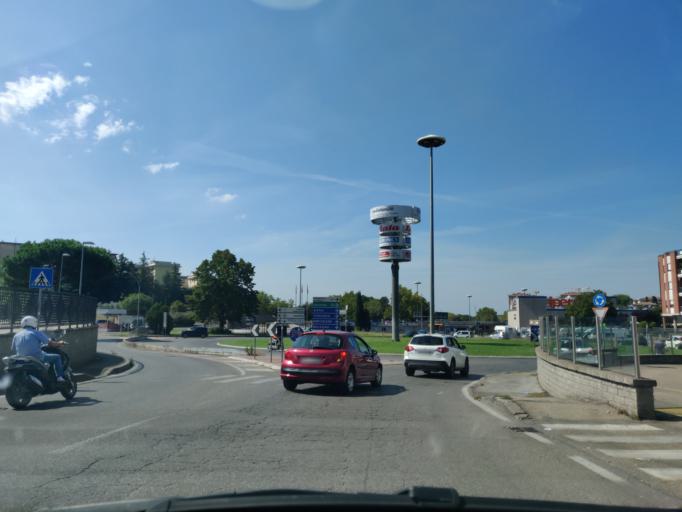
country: IT
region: Latium
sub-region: Provincia di Viterbo
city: Viterbo
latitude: 42.4271
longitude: 12.0995
